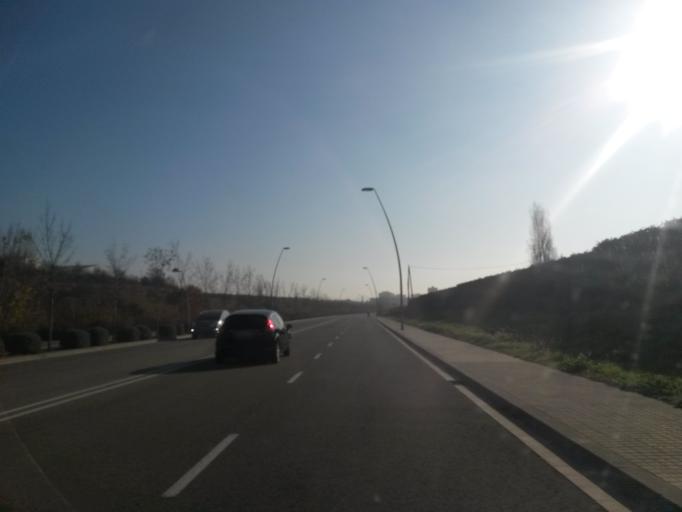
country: ES
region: Catalonia
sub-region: Provincia de Barcelona
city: Barbera del Valles
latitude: 41.5179
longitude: 2.1032
